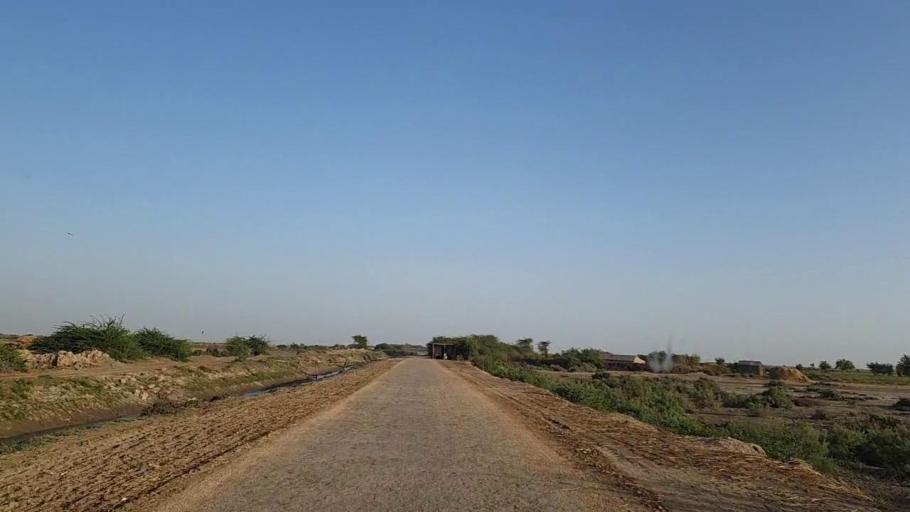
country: PK
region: Sindh
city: Jati
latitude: 24.4058
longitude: 68.3542
